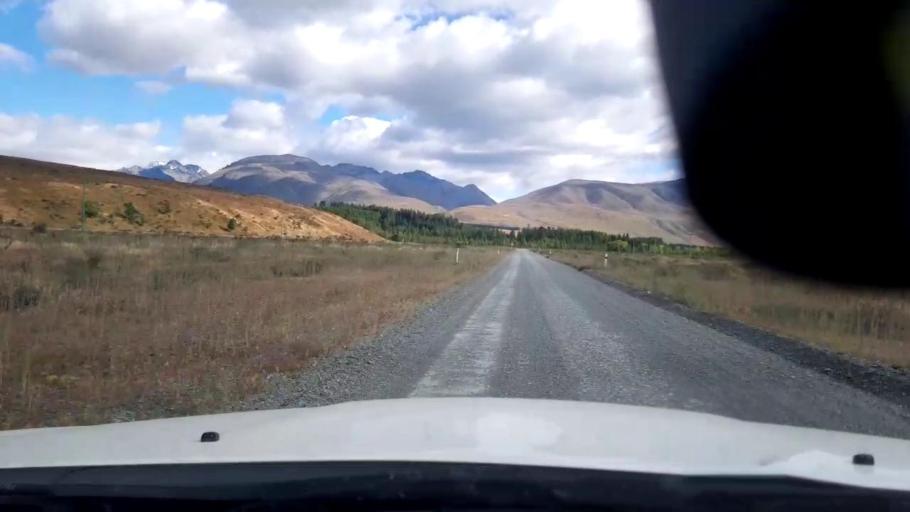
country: NZ
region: Canterbury
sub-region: Timaru District
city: Pleasant Point
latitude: -43.8824
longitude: 170.4667
